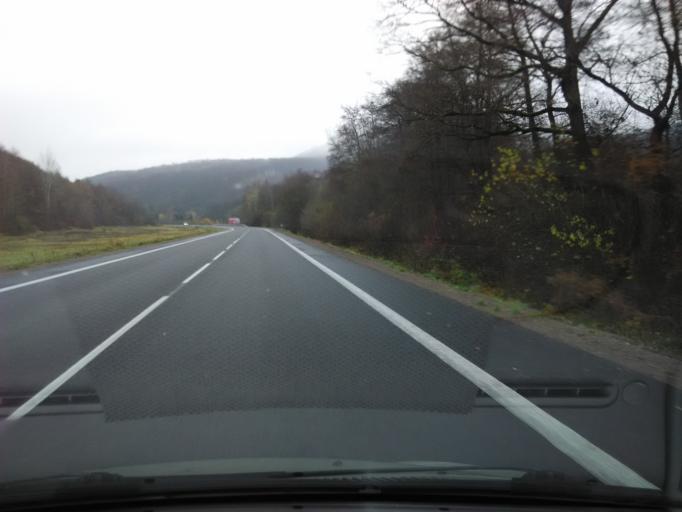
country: SK
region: Banskobystricky
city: Ziar nad Hronom
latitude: 48.6284
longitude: 18.8996
